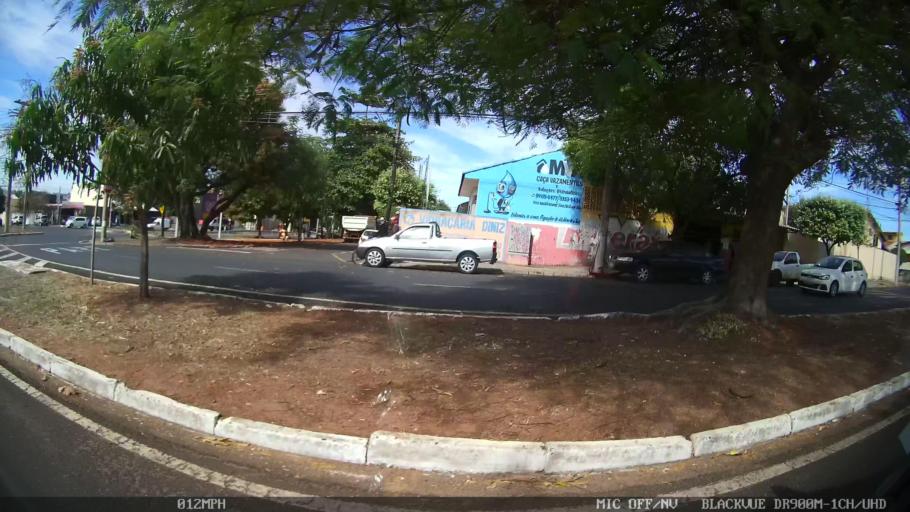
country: BR
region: Sao Paulo
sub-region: Sao Jose Do Rio Preto
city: Sao Jose do Rio Preto
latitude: -20.8315
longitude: -49.3514
